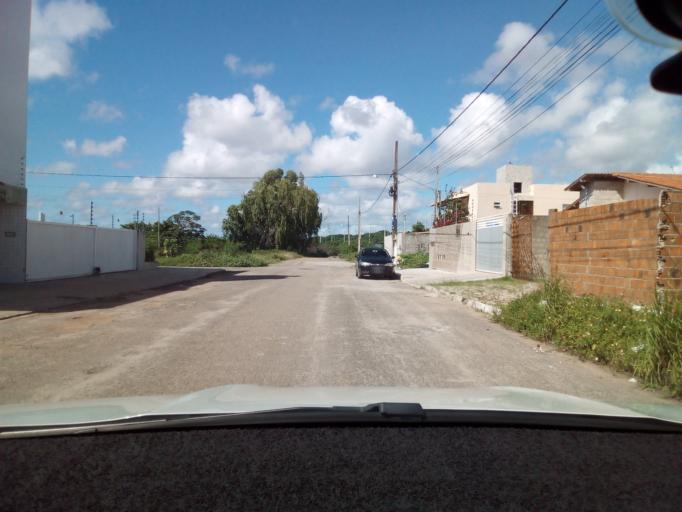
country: BR
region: Paraiba
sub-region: Joao Pessoa
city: Joao Pessoa
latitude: -7.0552
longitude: -34.8495
